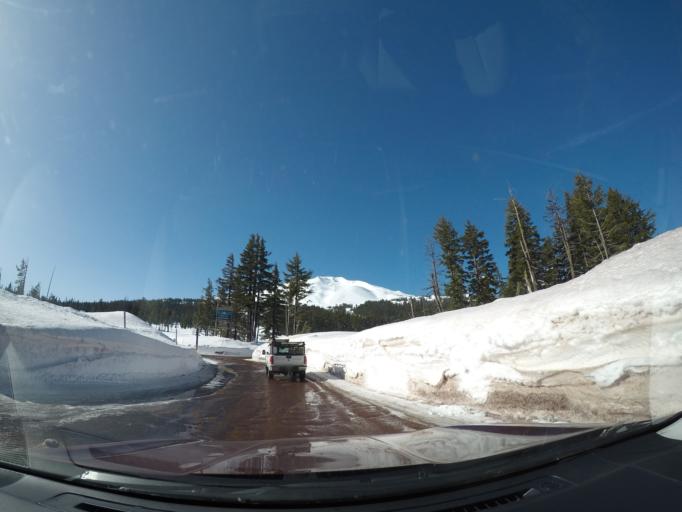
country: US
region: Oregon
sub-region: Deschutes County
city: Sunriver
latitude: 43.9948
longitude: -121.6604
